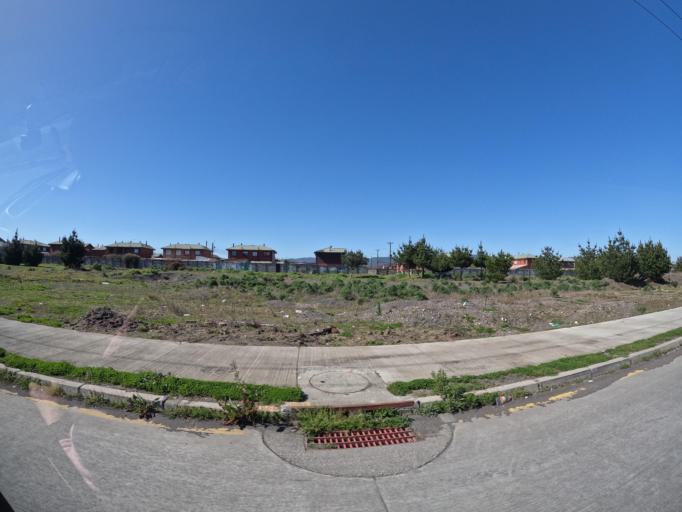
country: CL
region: Biobio
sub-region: Provincia de Concepcion
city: Concepcion
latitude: -36.8873
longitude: -73.1495
